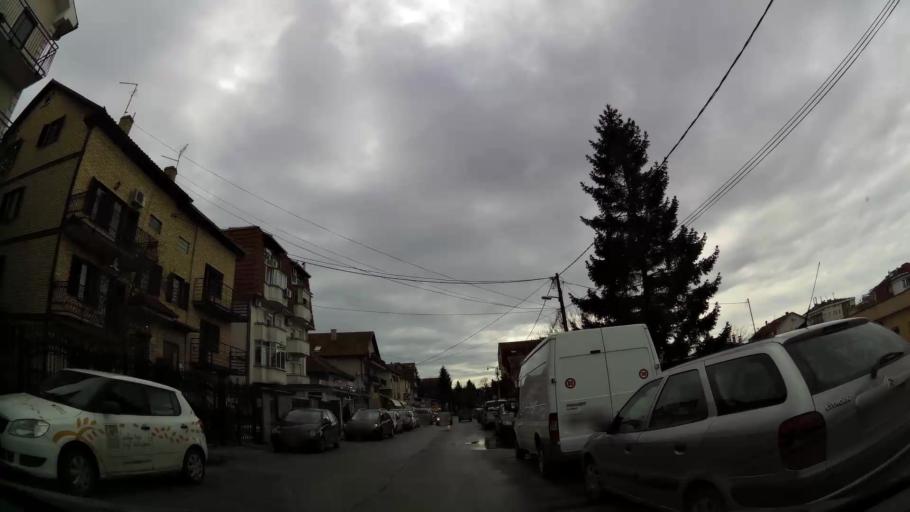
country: RS
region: Central Serbia
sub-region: Belgrade
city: Cukarica
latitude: 44.7518
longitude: 20.4077
